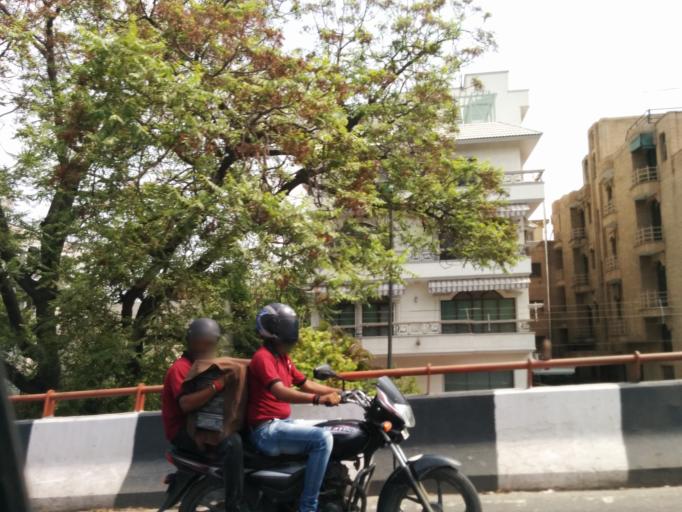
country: IN
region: NCT
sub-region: New Delhi
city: New Delhi
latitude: 28.5452
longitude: 77.1998
